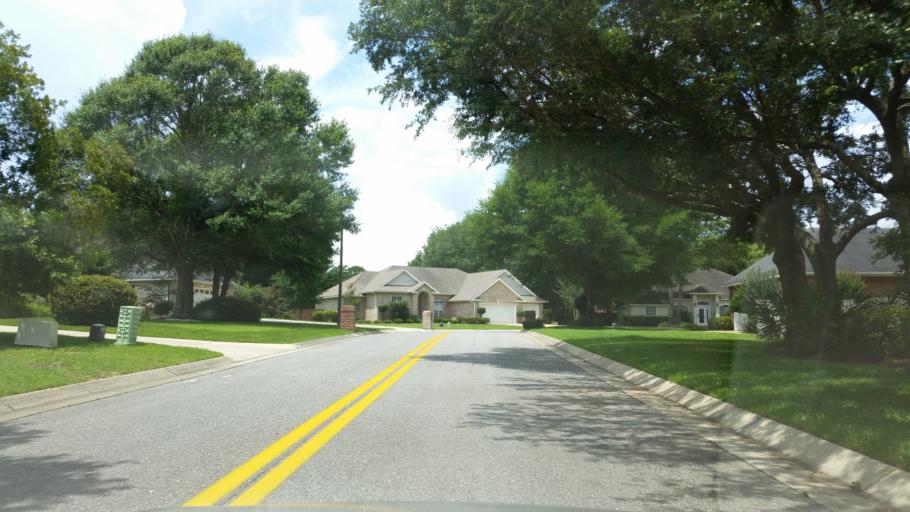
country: US
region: Florida
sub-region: Escambia County
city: Bellview
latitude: 30.4703
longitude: -87.2810
